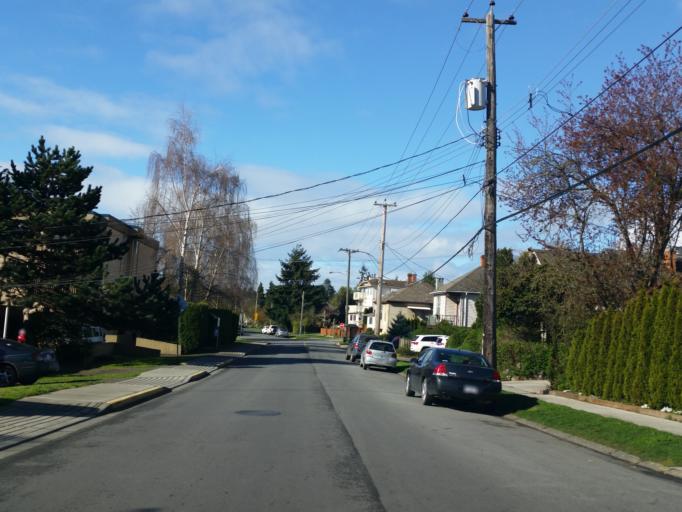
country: CA
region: British Columbia
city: Victoria
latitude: 48.4296
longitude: -123.3982
